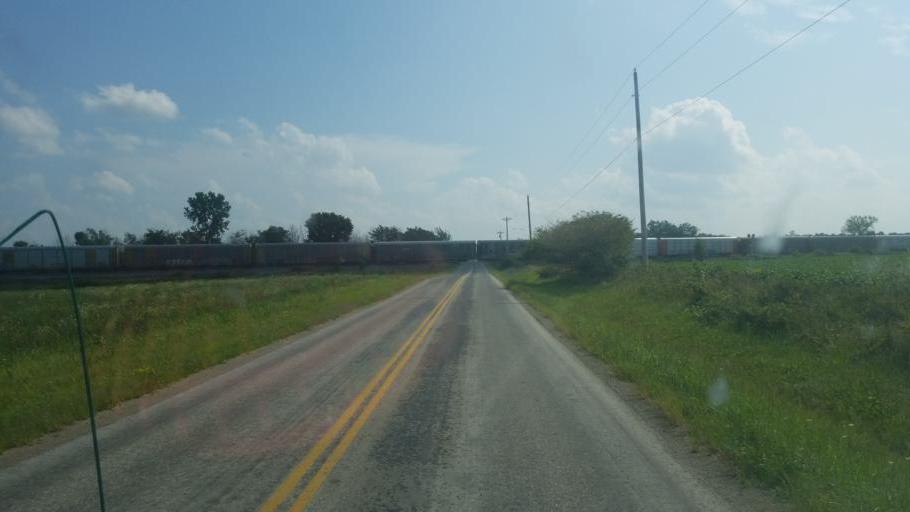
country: US
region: Ohio
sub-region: Wayne County
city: West Salem
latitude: 41.0474
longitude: -82.1818
